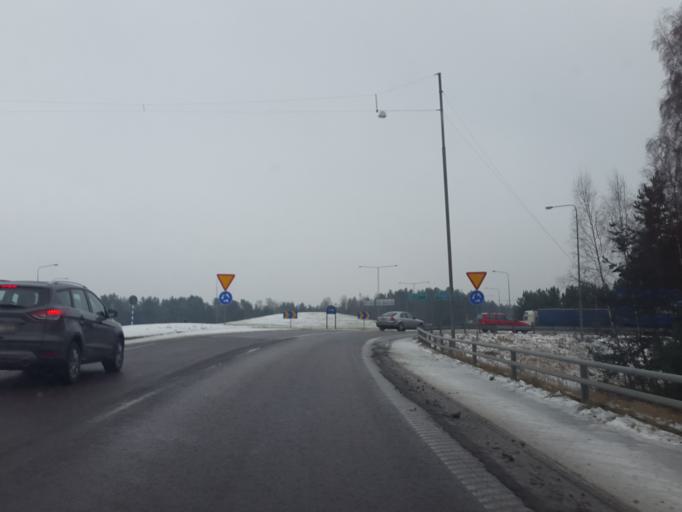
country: SE
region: Joenkoeping
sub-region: Jonkopings Kommun
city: Jonkoping
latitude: 57.7607
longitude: 14.1559
